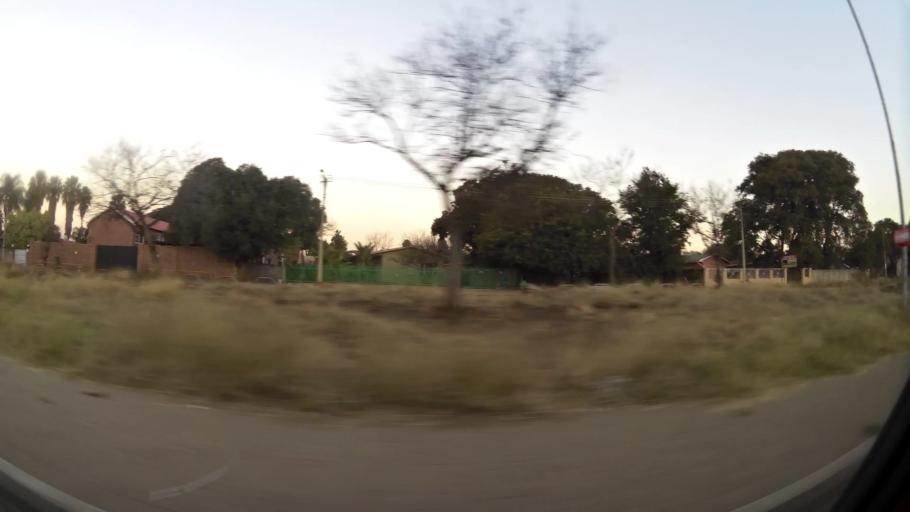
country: ZA
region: North-West
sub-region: Bojanala Platinum District Municipality
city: Rustenburg
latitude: -25.6541
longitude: 27.2463
